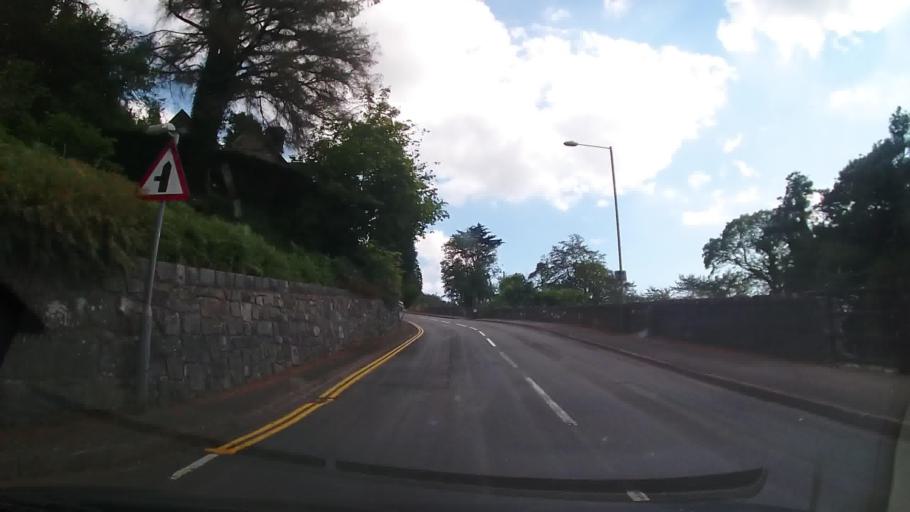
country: GB
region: Wales
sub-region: Gwynedd
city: Llanfair
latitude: 52.8543
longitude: -4.1123
